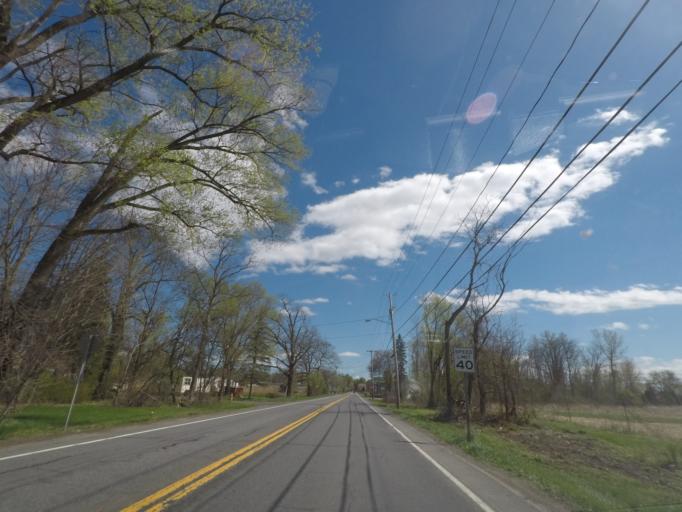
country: US
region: New York
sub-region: Columbia County
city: Oakdale
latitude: 42.2315
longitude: -73.7517
